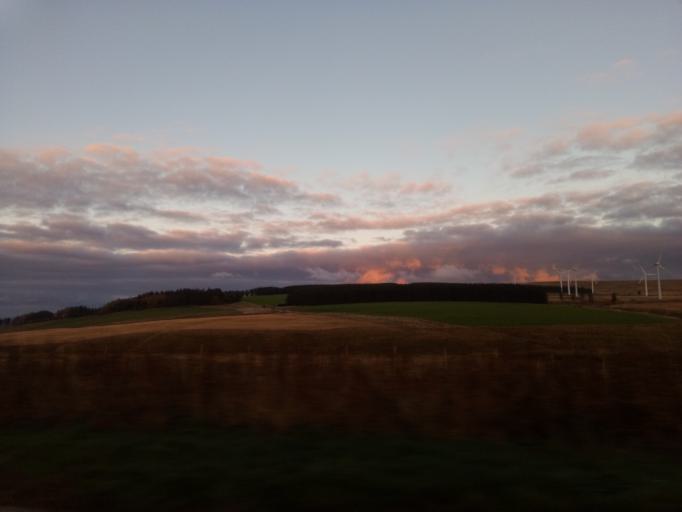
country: GB
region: Scotland
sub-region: East Lothian
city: Pencaitland
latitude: 55.8234
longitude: -2.8524
